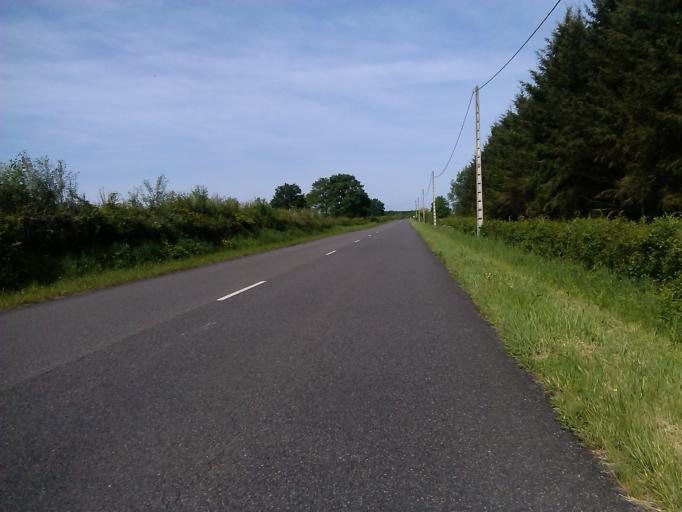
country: FR
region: Auvergne
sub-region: Departement de l'Allier
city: Dompierre-sur-Besbre
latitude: 46.5330
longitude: 3.6482
